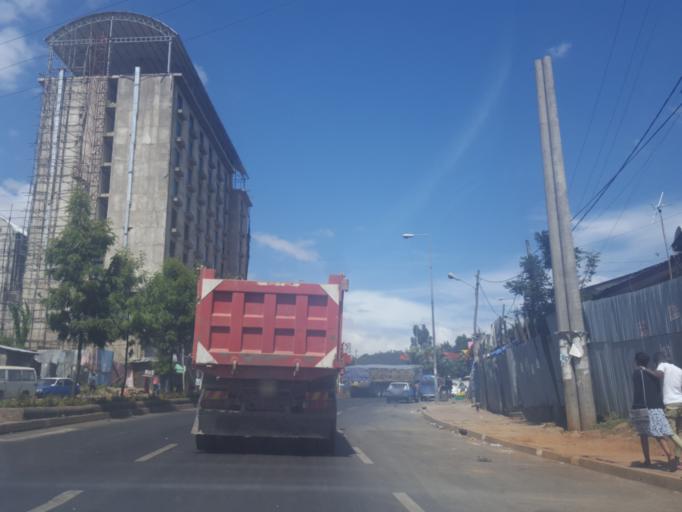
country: ET
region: Adis Abeba
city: Addis Ababa
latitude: 9.0646
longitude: 38.7330
